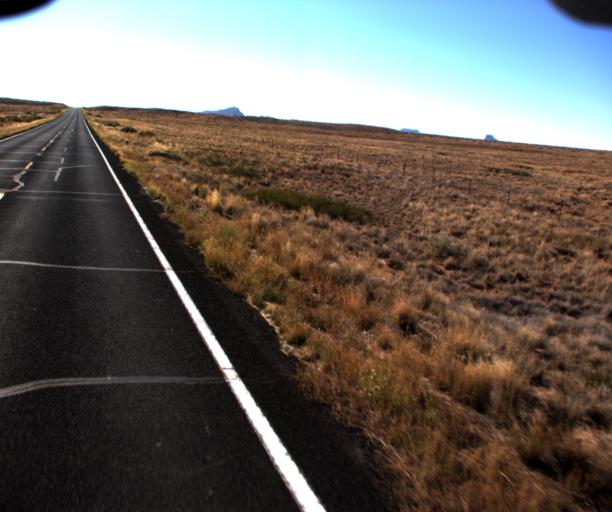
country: US
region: Arizona
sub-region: Navajo County
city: Dilkon
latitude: 35.5599
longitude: -110.4562
